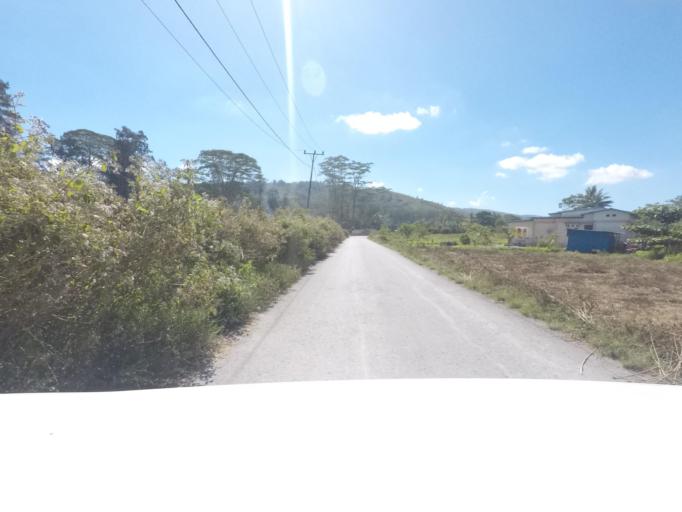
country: TL
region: Ermera
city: Gleno
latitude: -8.7137
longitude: 125.4337
